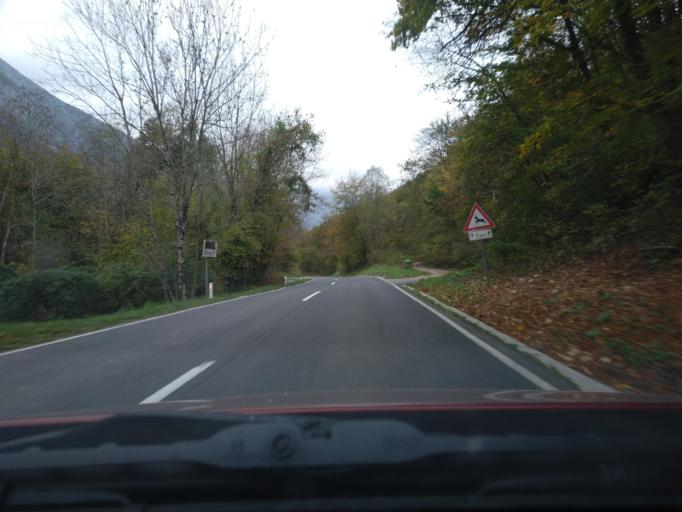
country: SI
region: Kobarid
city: Kobarid
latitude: 46.2760
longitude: 13.5618
